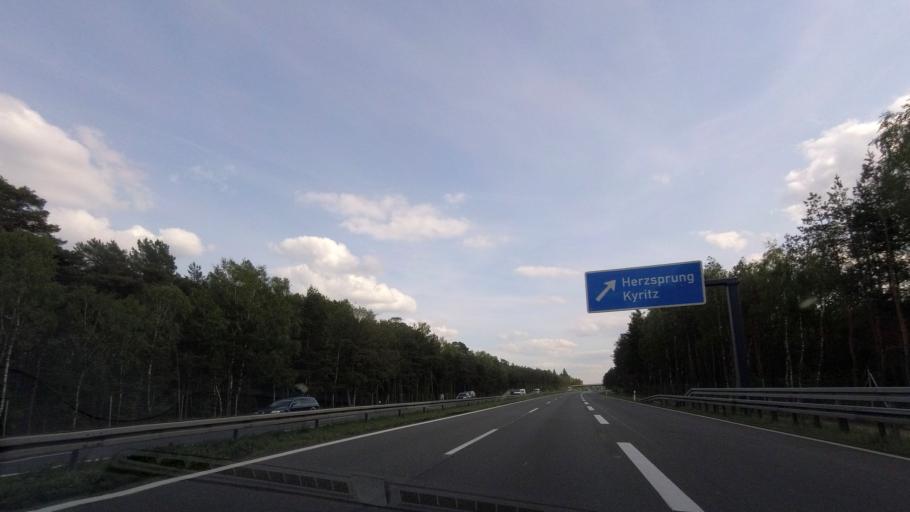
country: DE
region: Brandenburg
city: Wittstock
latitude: 53.0766
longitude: 12.5259
